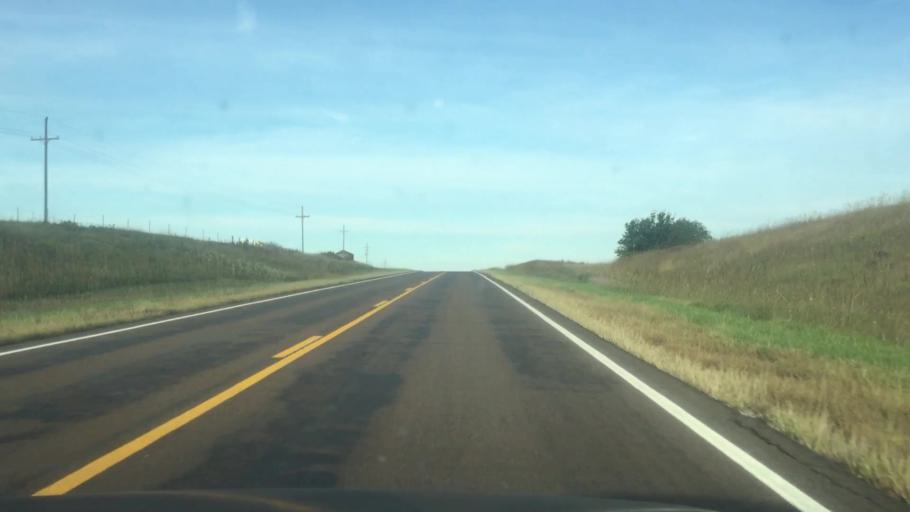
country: US
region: Nebraska
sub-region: Gage County
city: Wymore
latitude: 40.0458
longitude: -96.8254
